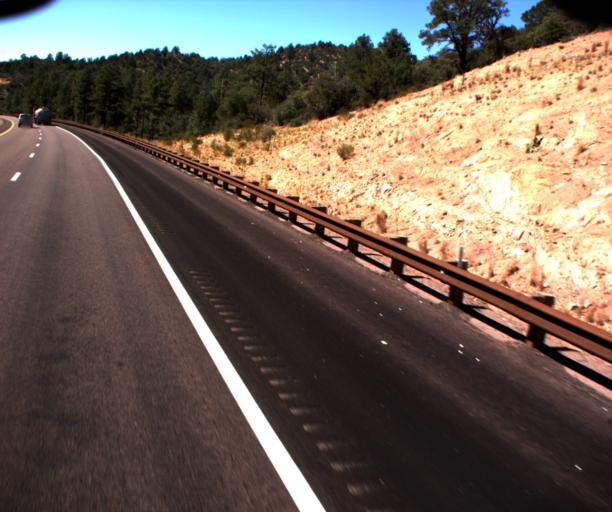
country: US
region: Arizona
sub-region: Gila County
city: Star Valley
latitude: 34.2942
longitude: -111.1311
